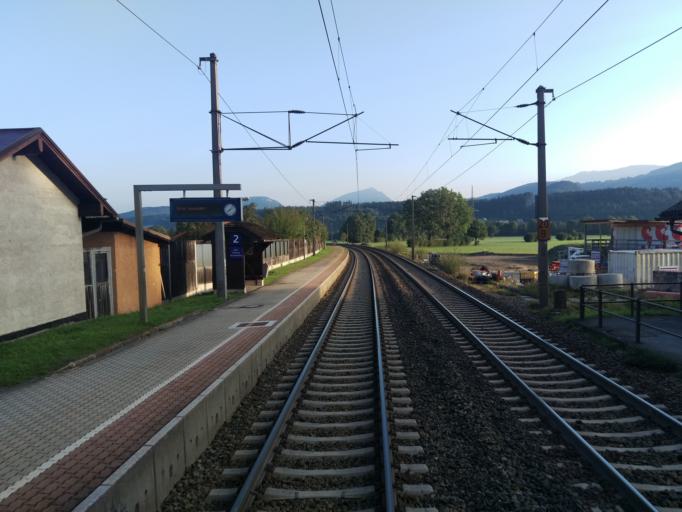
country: AT
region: Salzburg
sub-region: Politischer Bezirk Hallein
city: Adnet
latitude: 47.6643
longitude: 13.1241
